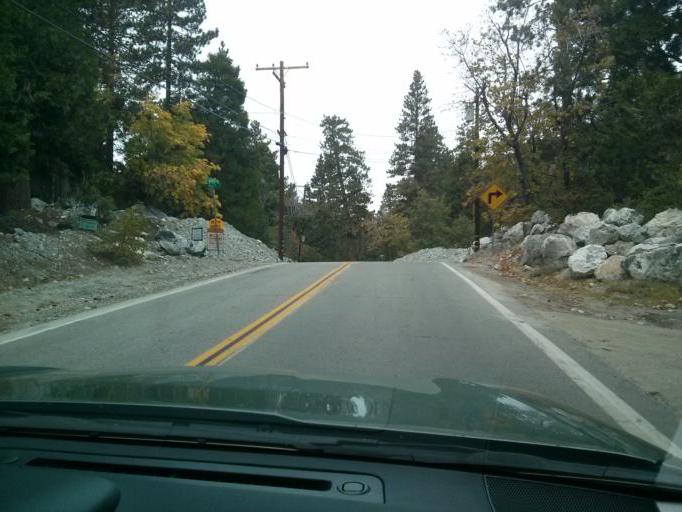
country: US
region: California
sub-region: Riverside County
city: Cherry Valley
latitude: 34.0829
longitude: -116.9040
